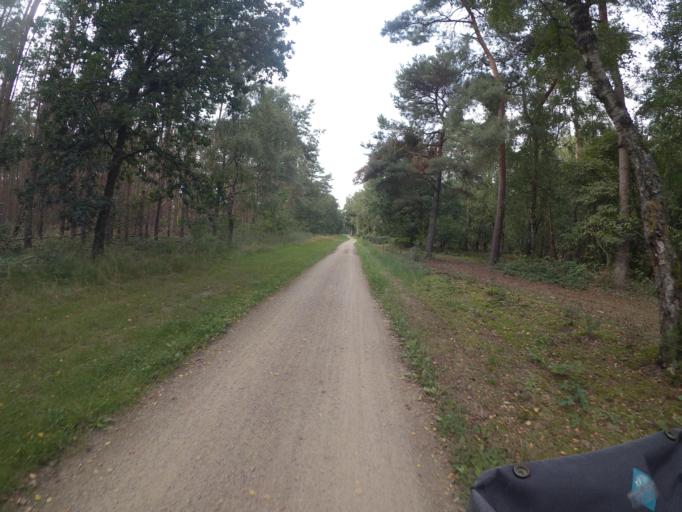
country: DE
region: North Rhine-Westphalia
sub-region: Regierungsbezirk Dusseldorf
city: Goch
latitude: 51.6204
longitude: 6.0723
